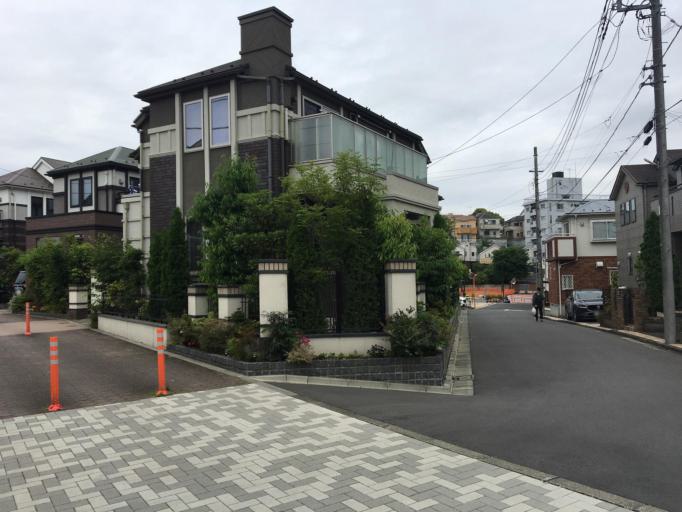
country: JP
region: Tokyo
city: Chofugaoka
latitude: 35.6608
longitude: 139.5756
